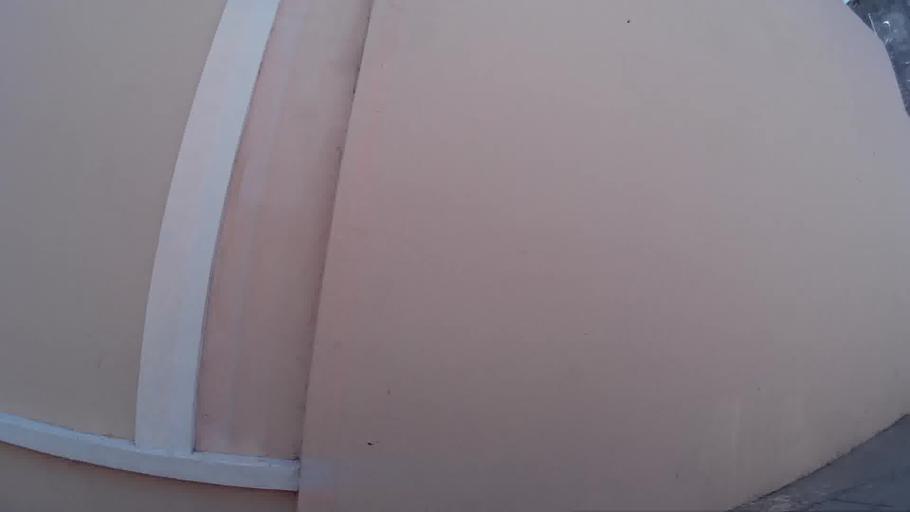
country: CO
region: Magdalena
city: Cienaga
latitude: 11.0115
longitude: -74.2523
